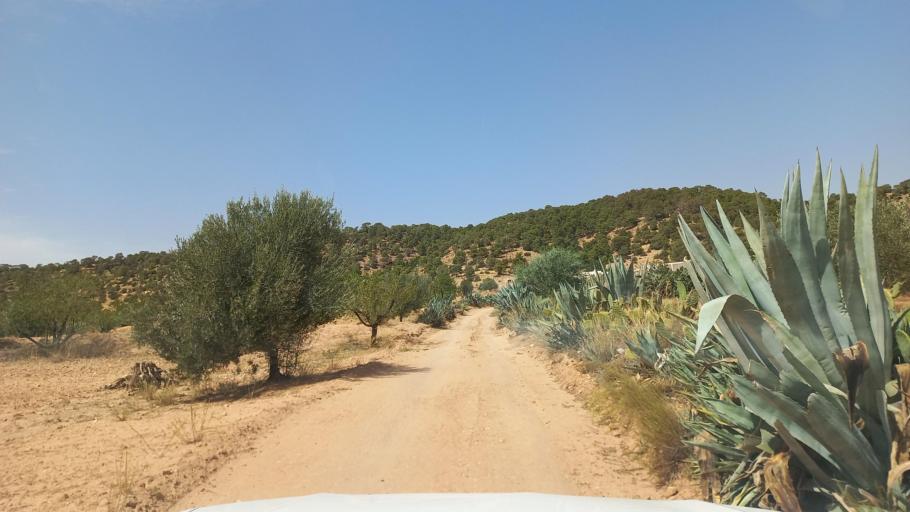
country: TN
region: Al Qasrayn
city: Kasserine
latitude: 35.3769
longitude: 8.9083
